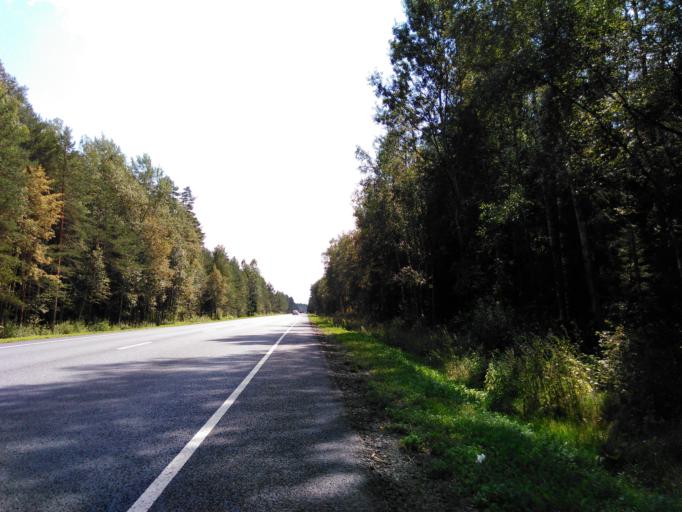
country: RU
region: Moskovskaya
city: Elektrogorsk
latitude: 56.0352
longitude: 38.7466
